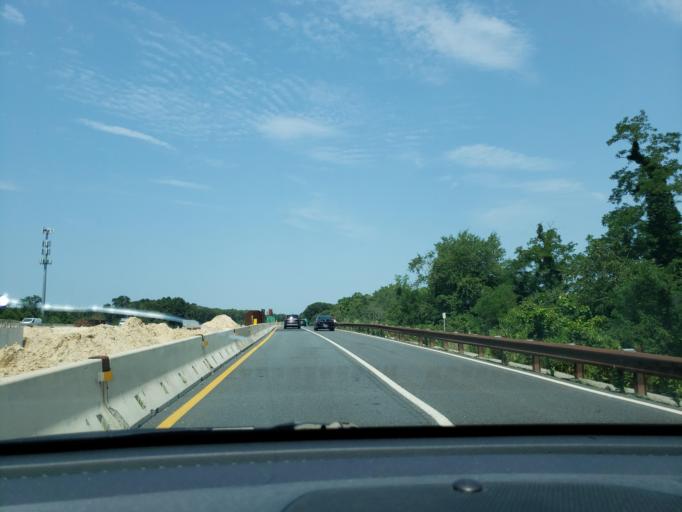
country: US
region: New Jersey
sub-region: Atlantic County
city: Linwood
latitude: 39.3669
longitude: -74.5847
